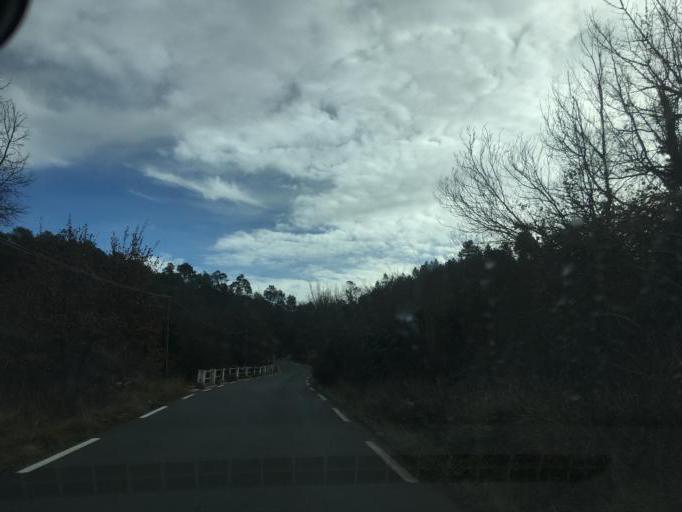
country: FR
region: Provence-Alpes-Cote d'Azur
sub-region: Departement du Var
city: Bras
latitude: 43.4587
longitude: 5.9672
